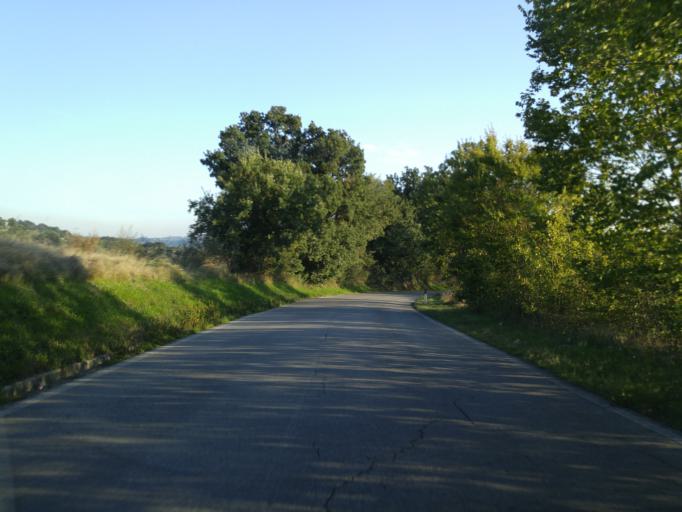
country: IT
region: The Marches
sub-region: Provincia di Pesaro e Urbino
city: Villa Ceccolini
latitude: 43.8537
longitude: 12.8793
